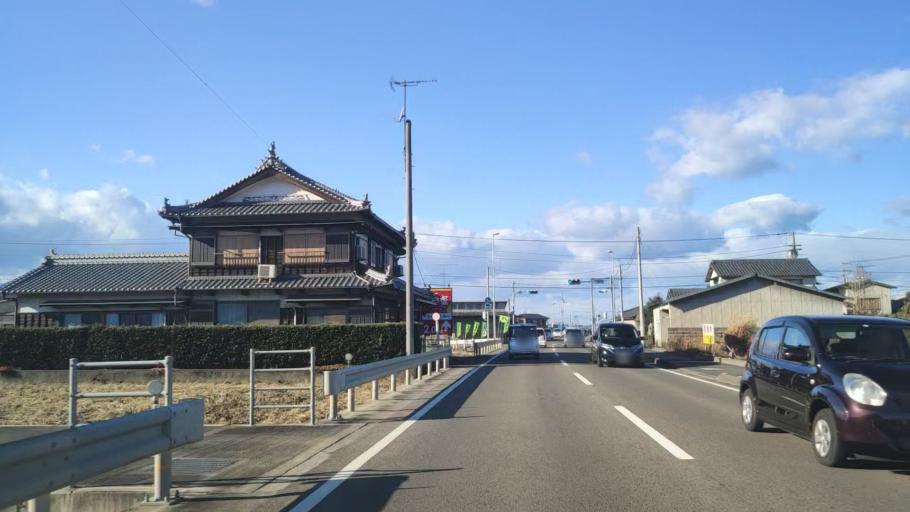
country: JP
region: Ehime
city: Saijo
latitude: 33.9160
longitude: 133.1054
